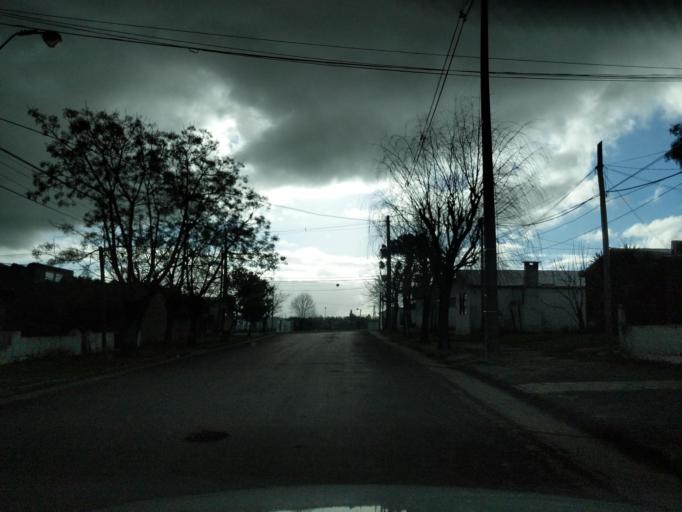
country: UY
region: Florida
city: Florida
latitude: -34.1041
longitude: -56.2210
